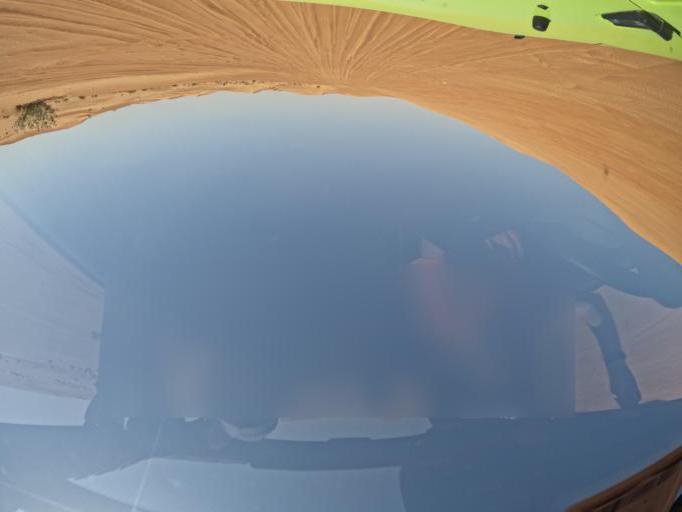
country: AE
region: Ash Shariqah
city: Adh Dhayd
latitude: 24.9831
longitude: 55.7231
